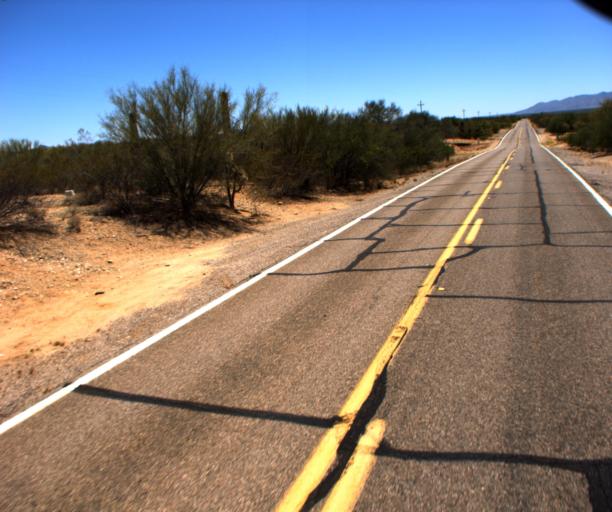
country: US
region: Arizona
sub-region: Pima County
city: Three Points
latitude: 31.9830
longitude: -111.3738
